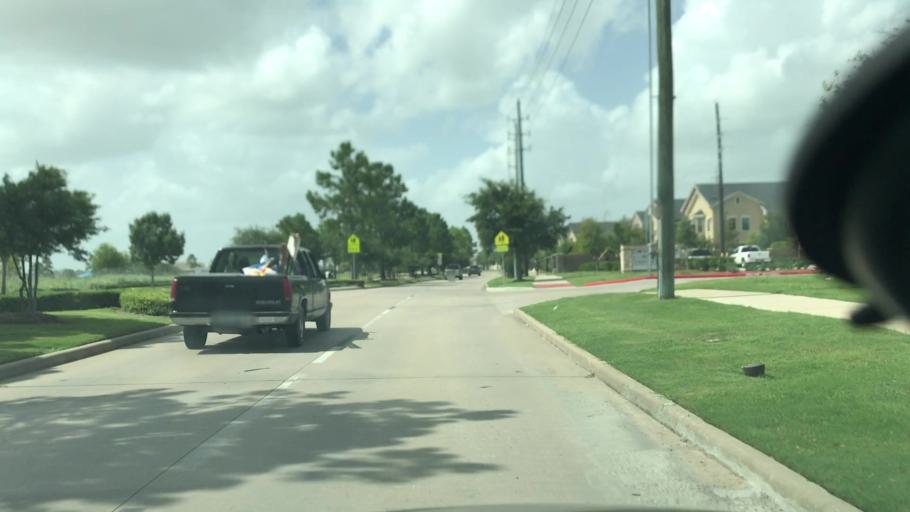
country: US
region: Texas
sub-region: Fort Bend County
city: Fresno
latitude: 29.5557
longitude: -95.4169
